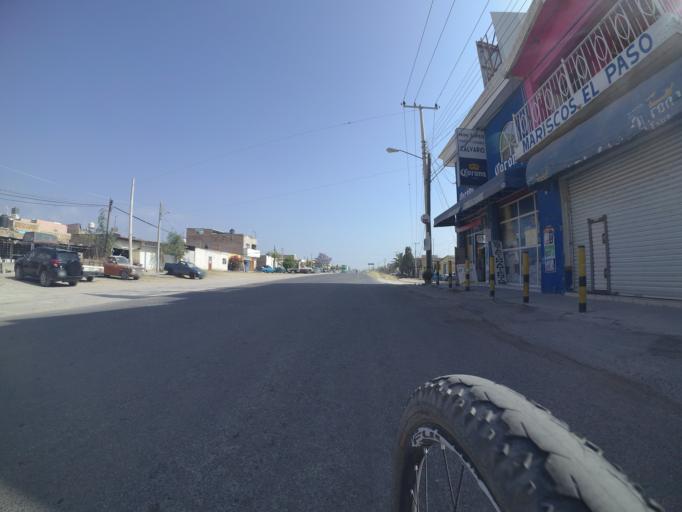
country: MX
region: Aguascalientes
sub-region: Jesus Maria
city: Jesus Maria
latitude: 21.9668
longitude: -102.3419
